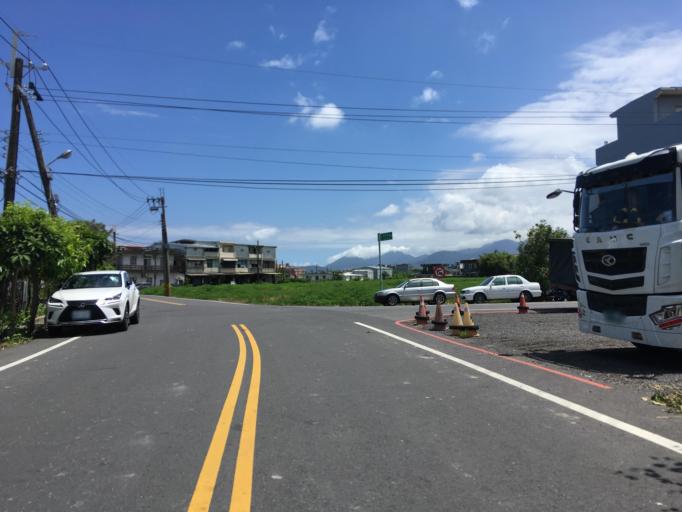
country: TW
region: Taiwan
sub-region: Yilan
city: Yilan
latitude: 24.6852
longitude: 121.8021
